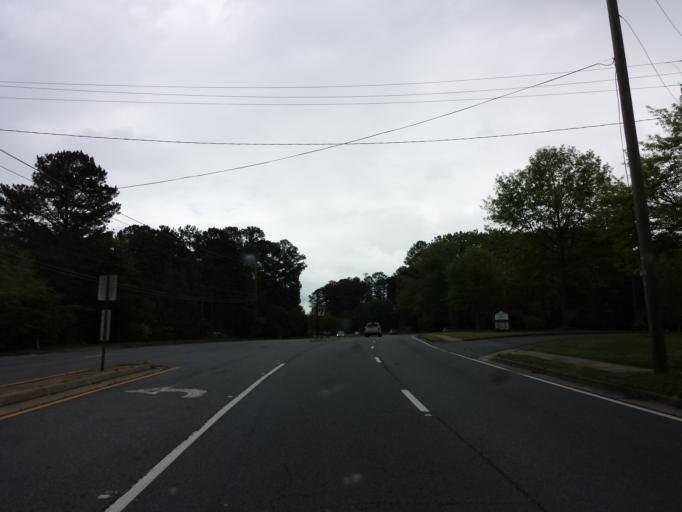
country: US
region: Georgia
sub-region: Cobb County
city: Marietta
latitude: 34.0159
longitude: -84.5046
